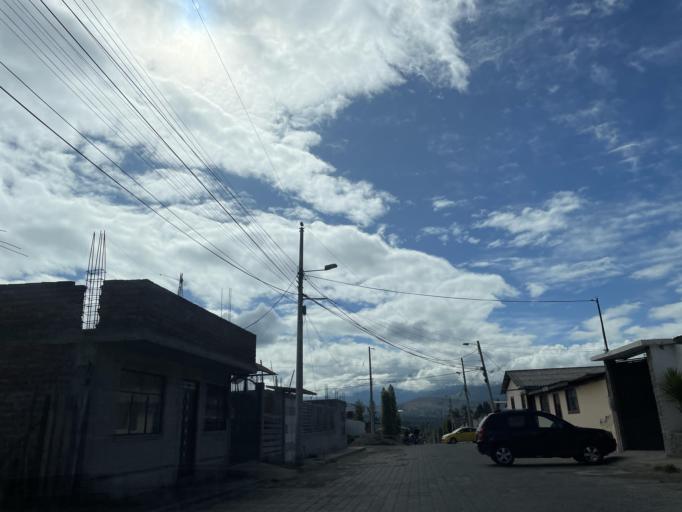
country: EC
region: Chimborazo
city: Guano
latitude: -1.6088
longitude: -78.6290
